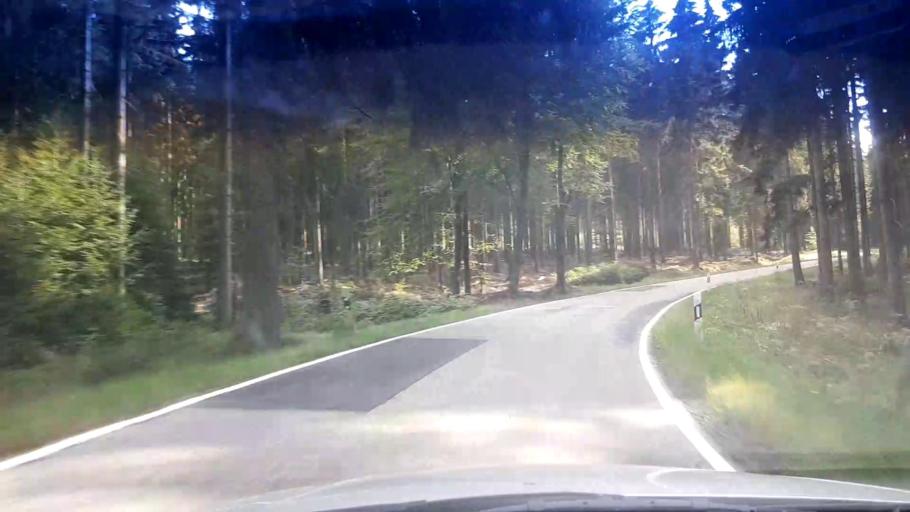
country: DE
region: Bavaria
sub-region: Upper Palatinate
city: Neualbenreuth
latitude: 49.9446
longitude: 12.4191
